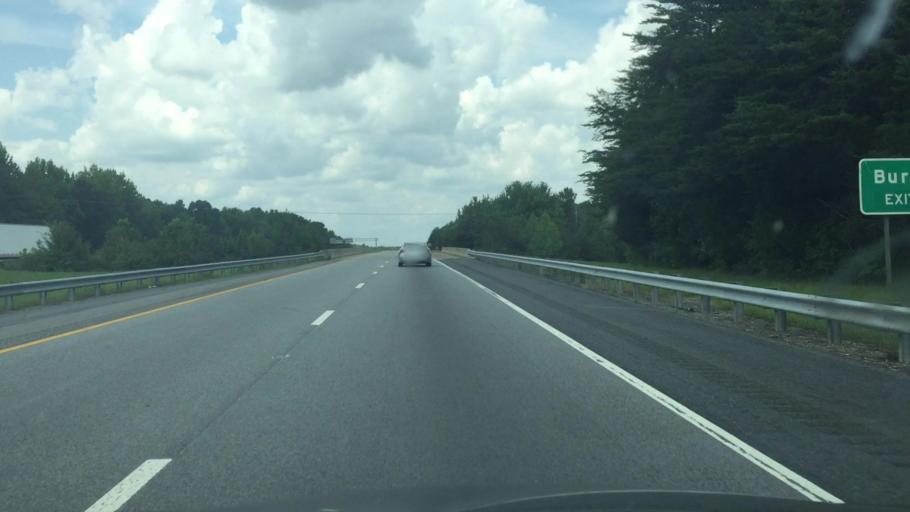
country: US
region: North Carolina
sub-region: Guilford County
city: Pleasant Garden
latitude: 35.9865
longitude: -79.8249
